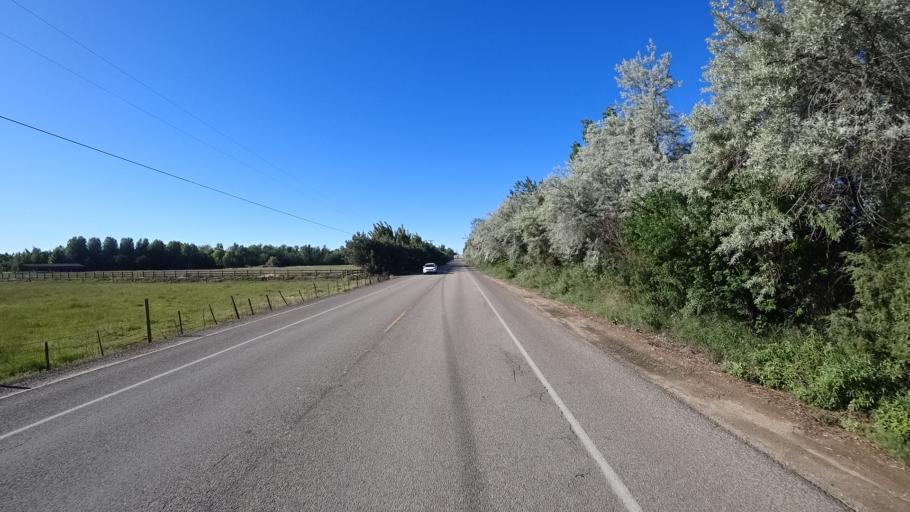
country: US
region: Idaho
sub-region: Ada County
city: Eagle
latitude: 43.6773
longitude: -116.4137
